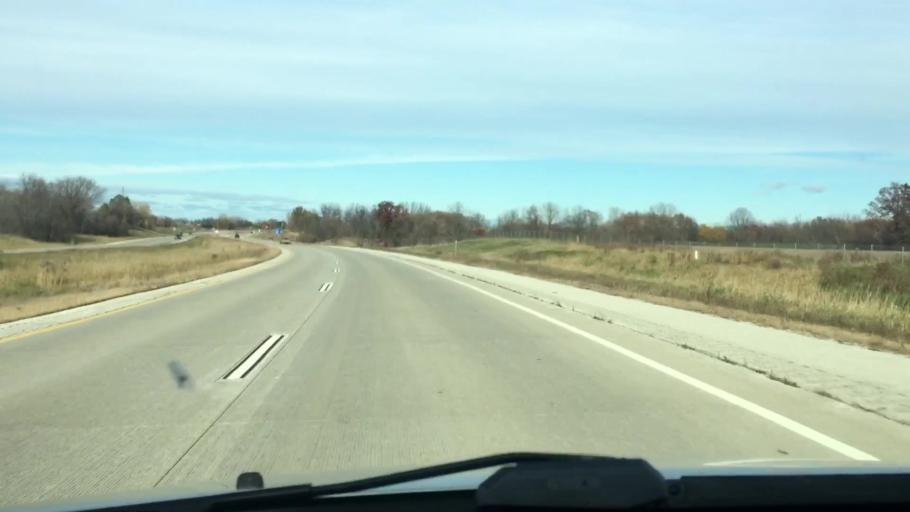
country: US
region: Wisconsin
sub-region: Kewaunee County
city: Luxemburg
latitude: 44.6407
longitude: -87.7533
